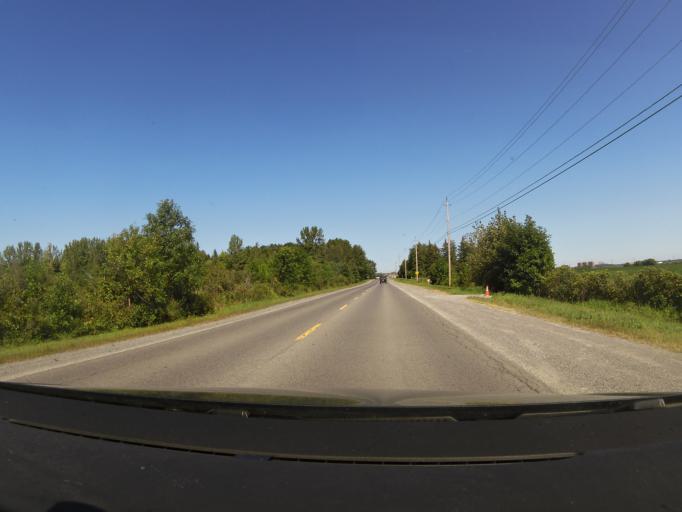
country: CA
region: Ontario
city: Bells Corners
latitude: 45.3051
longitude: -75.9535
